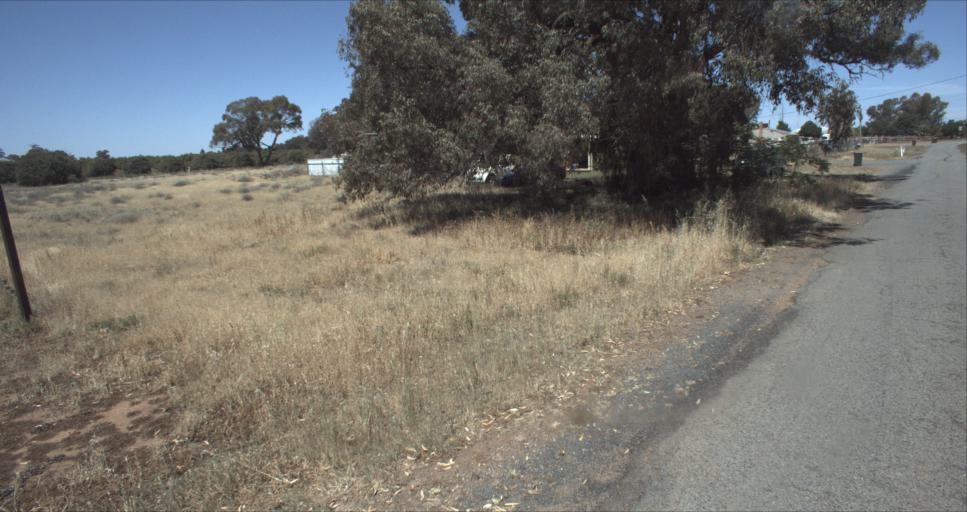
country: AU
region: New South Wales
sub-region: Leeton
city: Leeton
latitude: -34.5287
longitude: 146.3331
